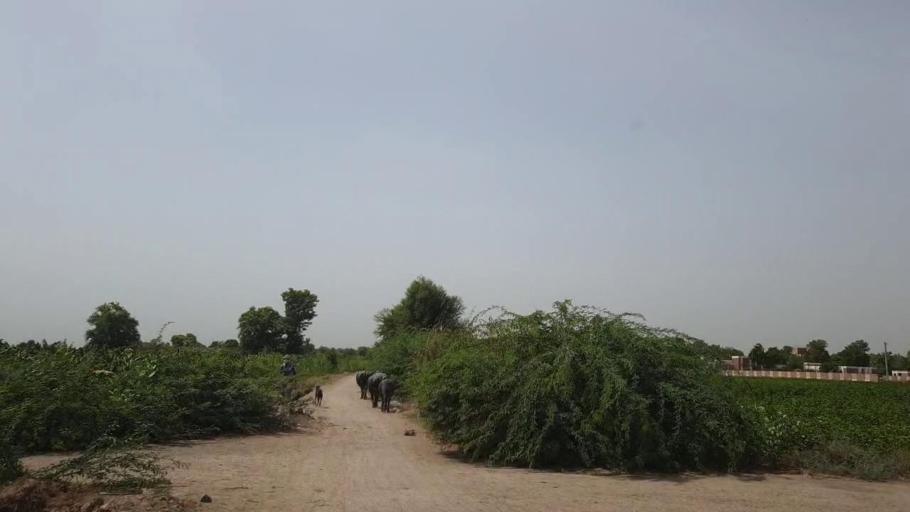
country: PK
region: Sindh
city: Sakrand
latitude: 26.1278
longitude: 68.2864
